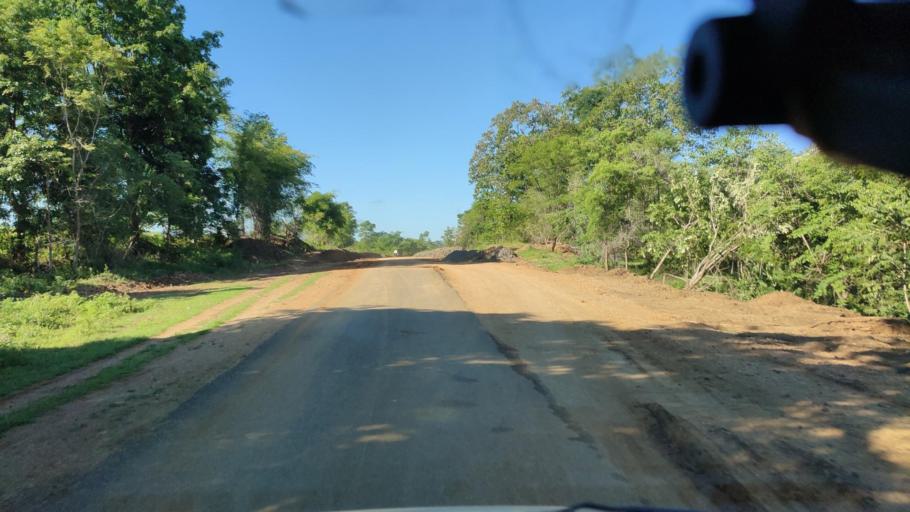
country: MM
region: Magway
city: Magway
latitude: 19.7306
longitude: 94.9412
